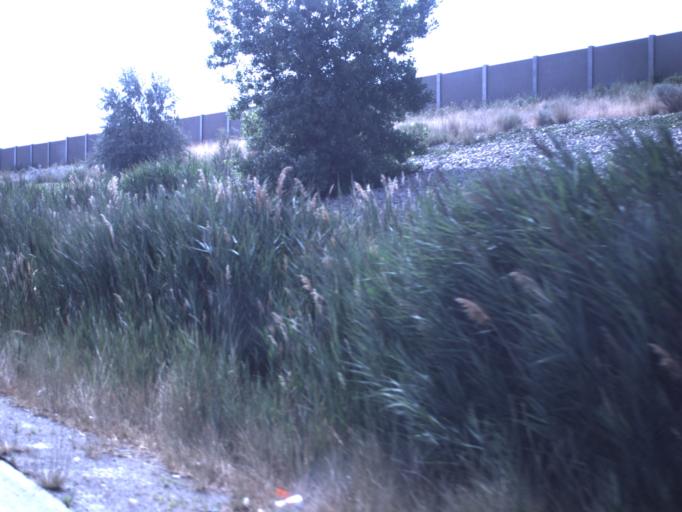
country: US
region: Utah
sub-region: Salt Lake County
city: Bluffdale
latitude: 40.4967
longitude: -111.9167
